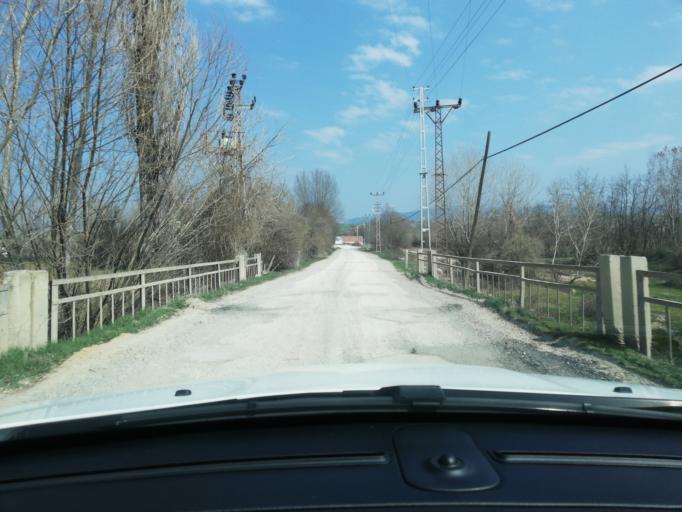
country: TR
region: Kastamonu
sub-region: Cide
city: Kastamonu
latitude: 41.4536
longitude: 33.7670
